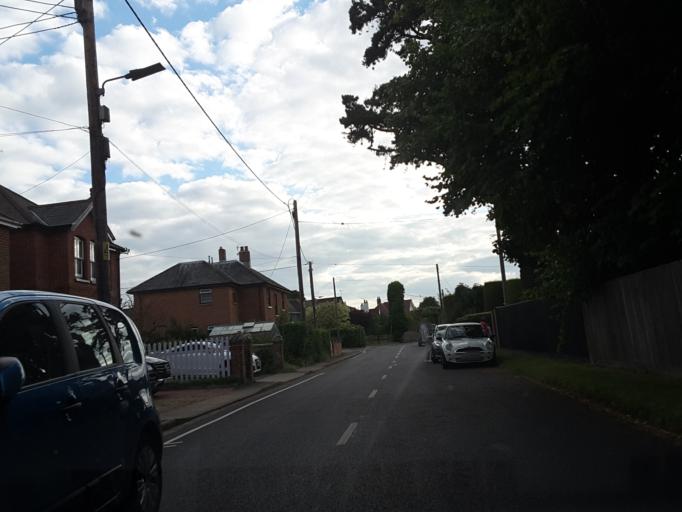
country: GB
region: England
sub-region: Isle of Wight
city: Bembridge
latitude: 50.6879
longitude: -1.0744
